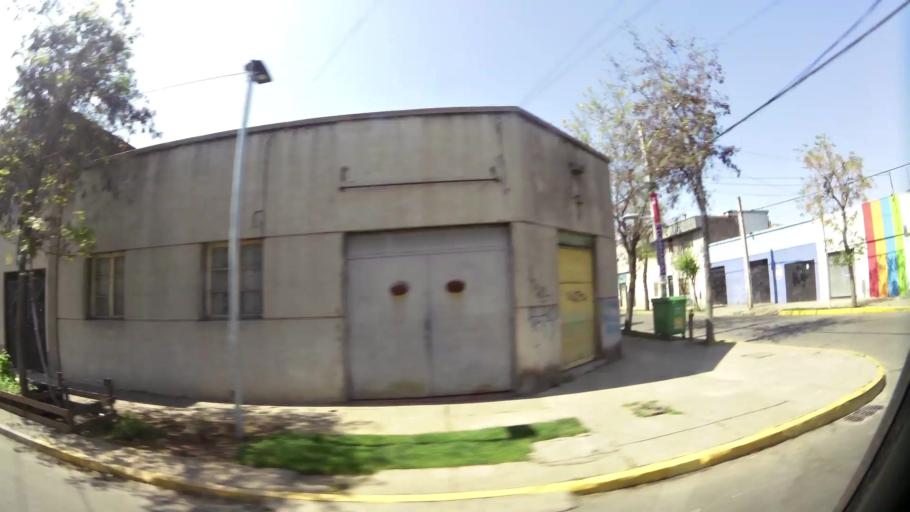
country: CL
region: Santiago Metropolitan
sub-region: Provincia de Santiago
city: Santiago
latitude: -33.4600
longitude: -70.6349
